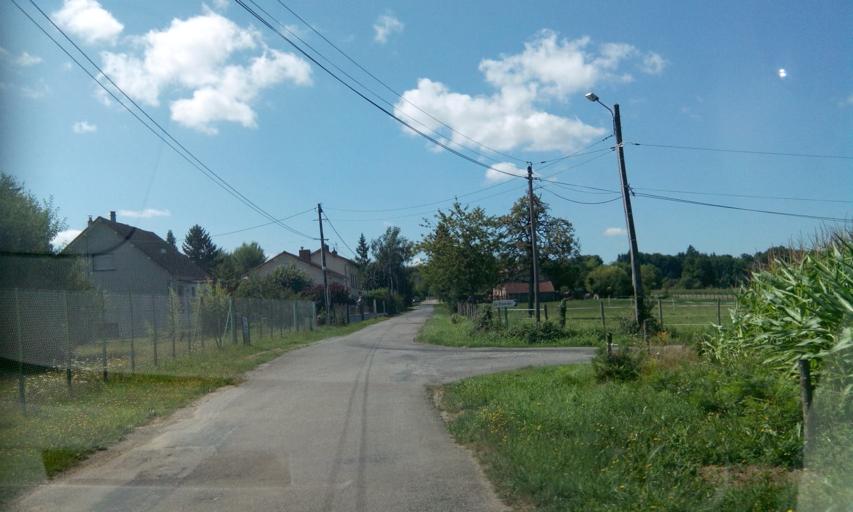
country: FR
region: Limousin
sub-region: Departement de la Haute-Vienne
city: Saint-Leonard-de-Noblat
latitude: 45.8125
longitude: 1.4669
